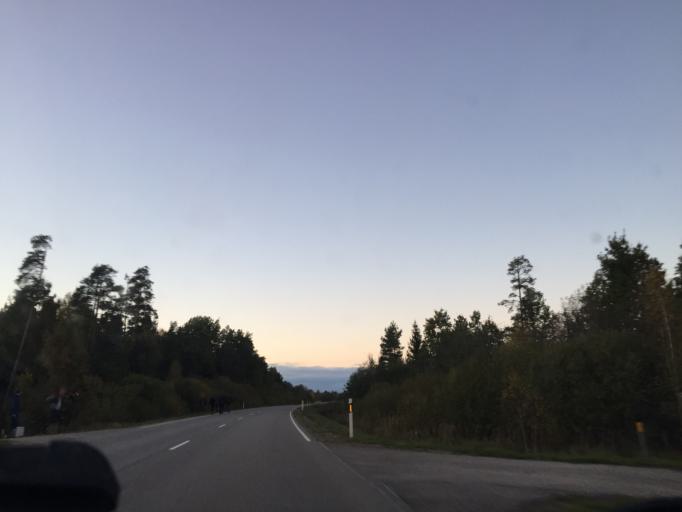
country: LV
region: Talsu Rajons
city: Sabile
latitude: 56.9412
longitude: 22.6538
